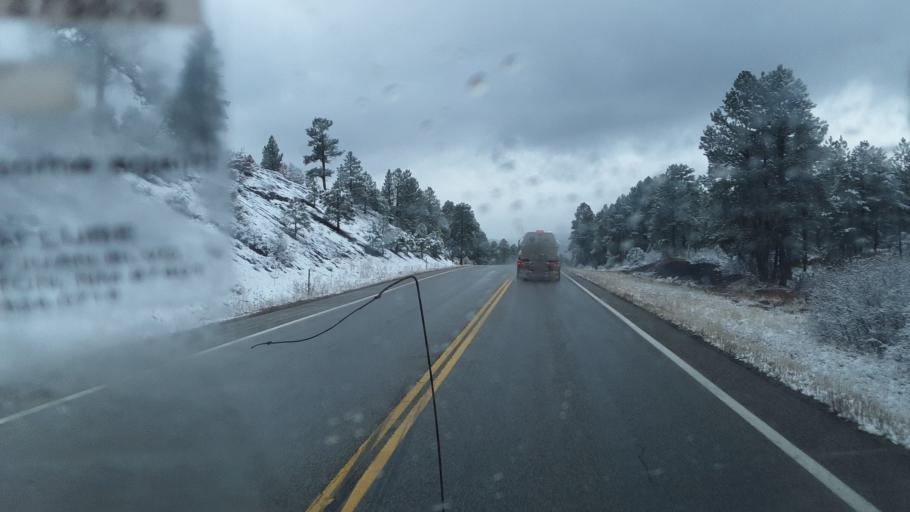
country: US
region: Colorado
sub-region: Archuleta County
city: Pagosa Springs
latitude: 37.2129
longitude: -107.2775
